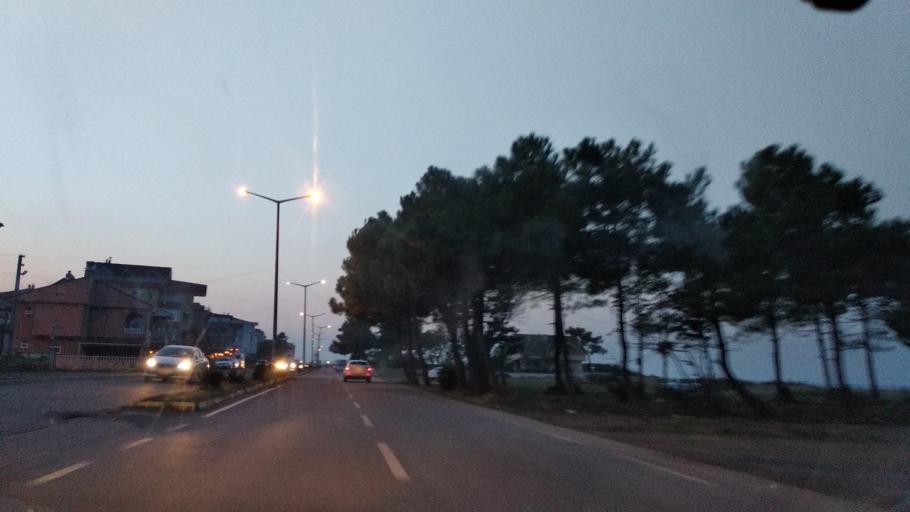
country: TR
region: Sakarya
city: Karasu
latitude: 41.0948
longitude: 30.7335
